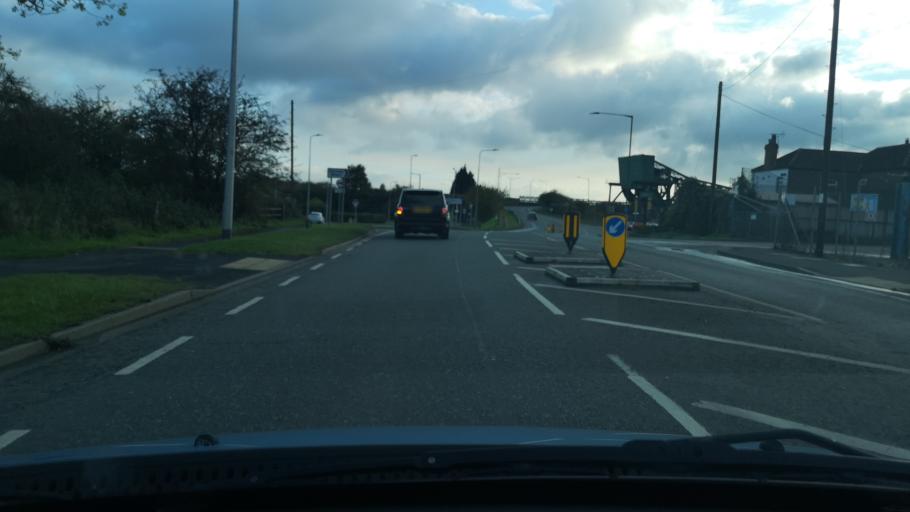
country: GB
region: England
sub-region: North Lincolnshire
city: Gunness
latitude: 53.5879
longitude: -0.7286
